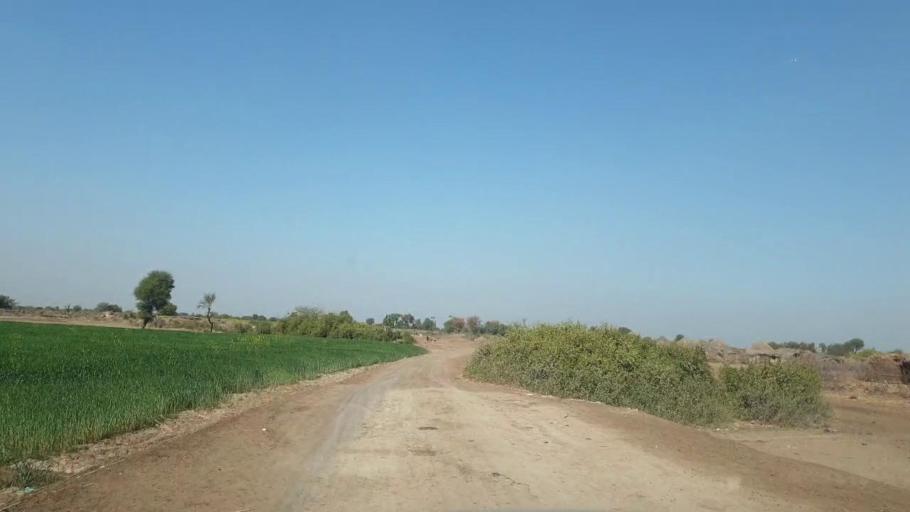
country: PK
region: Sindh
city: Tando Adam
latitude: 25.6479
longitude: 68.6863
